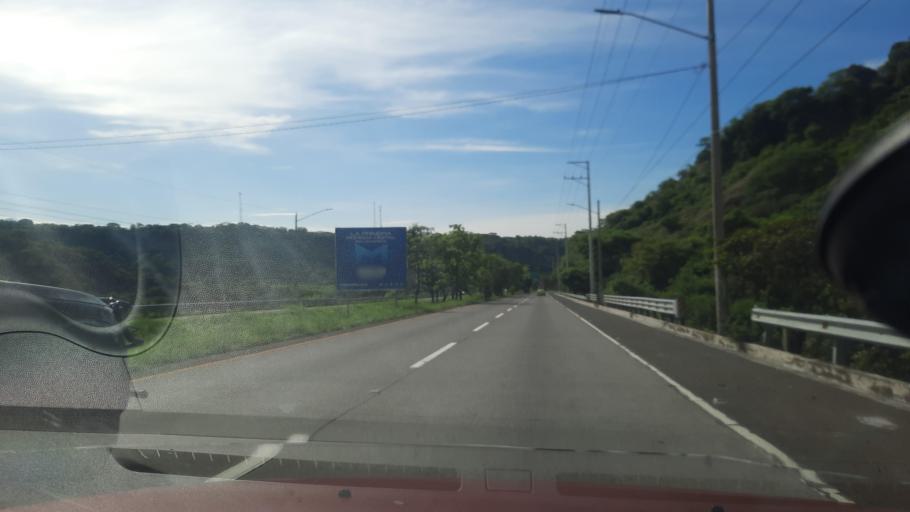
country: SV
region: La Paz
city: Olocuilta
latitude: 13.5141
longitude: -89.0964
